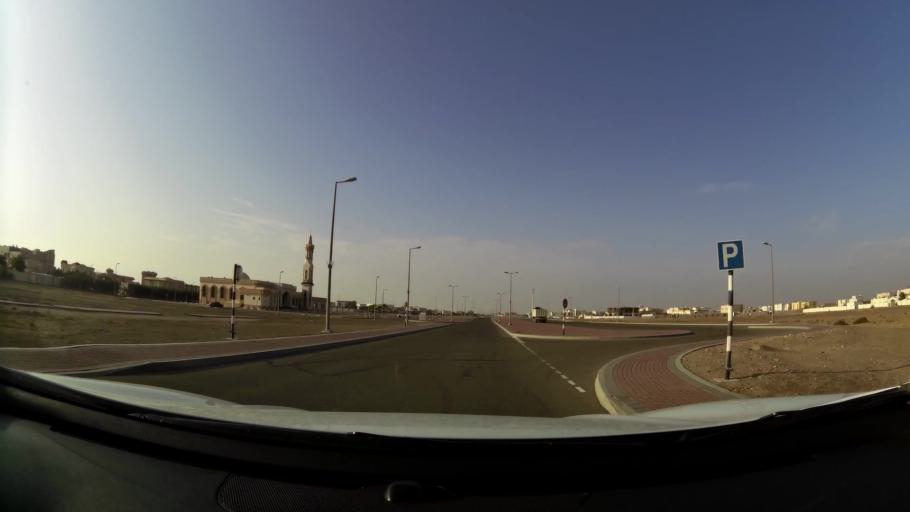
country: AE
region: Abu Dhabi
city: Al Ain
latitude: 24.0977
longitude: 55.8357
